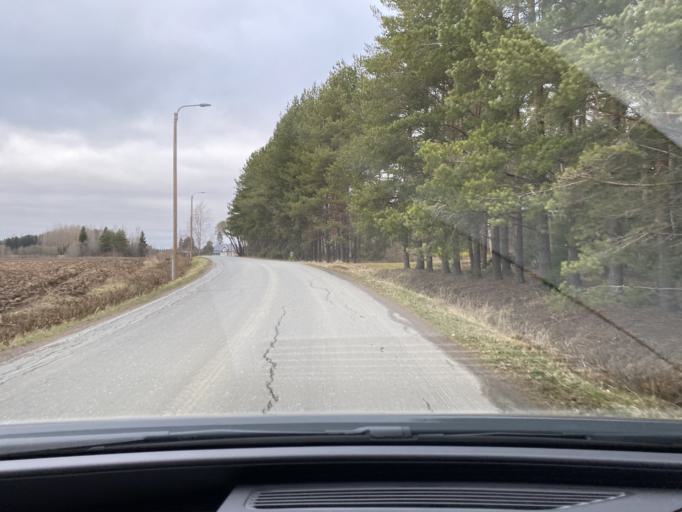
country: FI
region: Satakunta
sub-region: Pori
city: Huittinen
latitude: 61.1650
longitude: 22.7250
